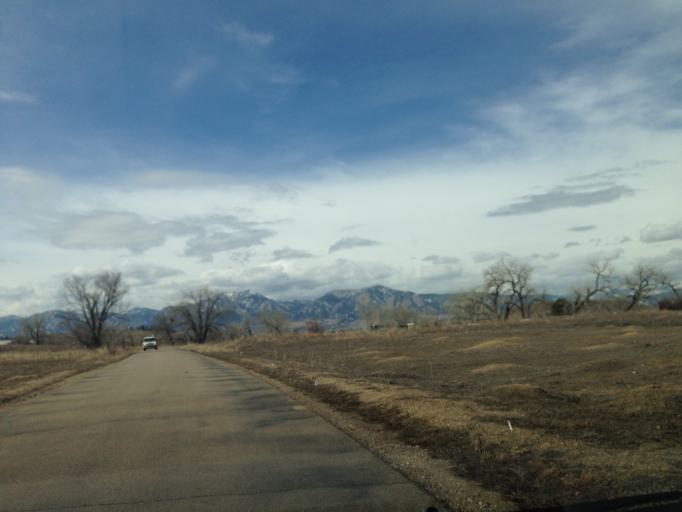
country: US
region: Colorado
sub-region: Boulder County
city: Gunbarrel
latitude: 40.0242
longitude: -105.1803
